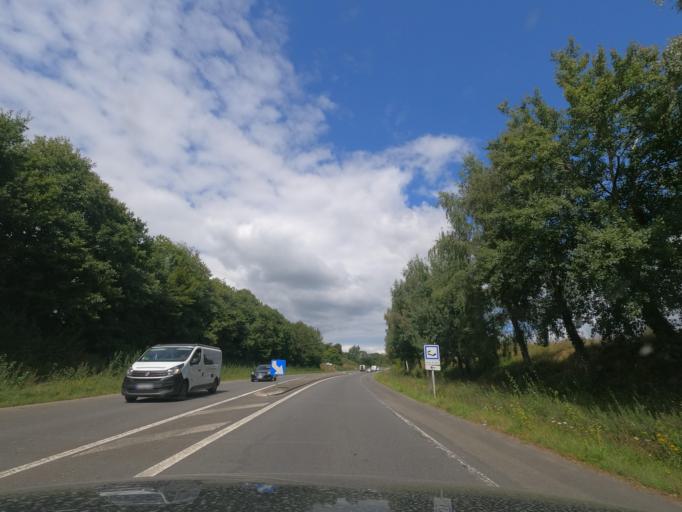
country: FR
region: Brittany
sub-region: Departement d'Ille-et-Vilaine
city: Lecousse
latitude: 48.3537
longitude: -1.2303
